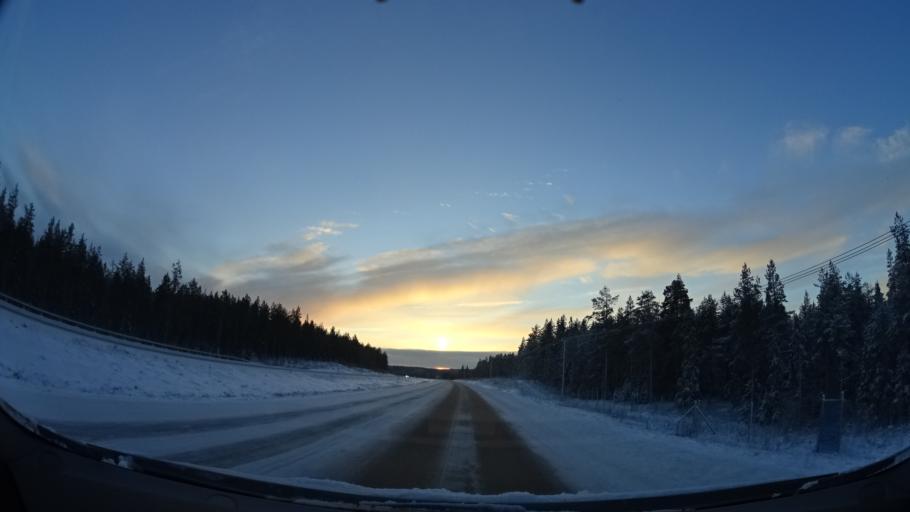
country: SE
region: Vaesterbotten
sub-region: Skelleftea Kommun
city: Kage
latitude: 64.7976
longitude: 21.0252
